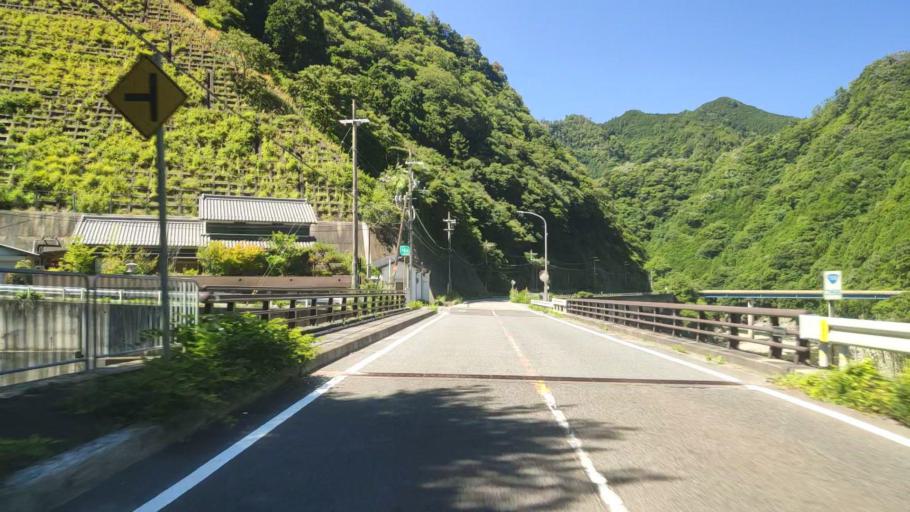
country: JP
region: Nara
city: Yoshino-cho
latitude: 34.3066
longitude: 135.9920
